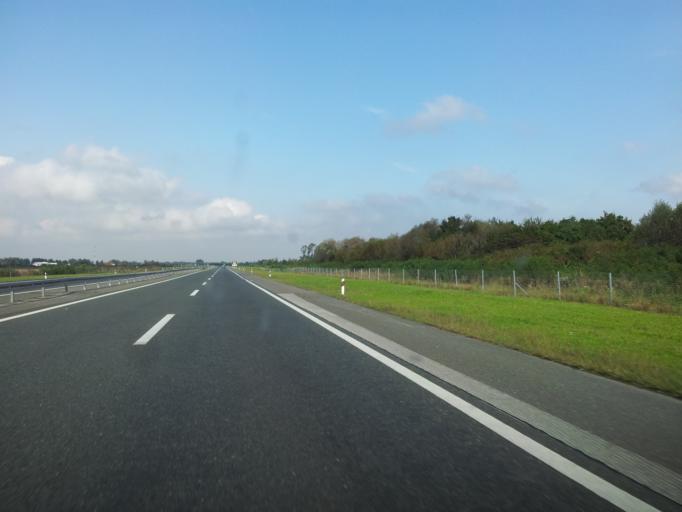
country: HR
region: Brodsko-Posavska
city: Luzani
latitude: 45.1583
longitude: 17.7245
